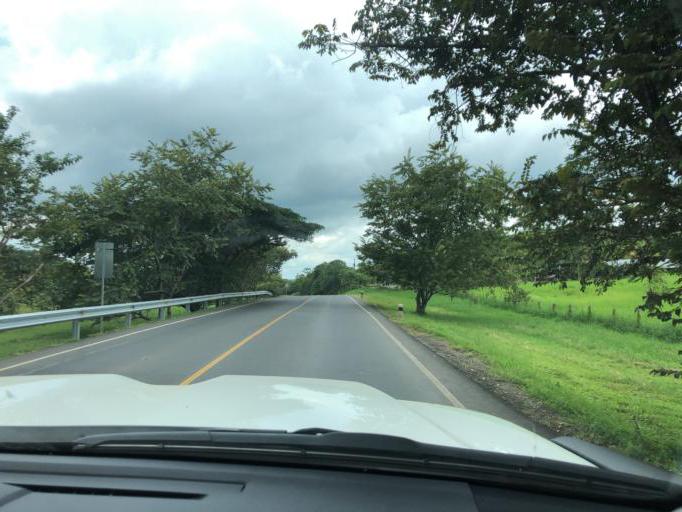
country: NI
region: Chontales
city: Santo Tomas
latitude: 12.0622
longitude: -85.0511
